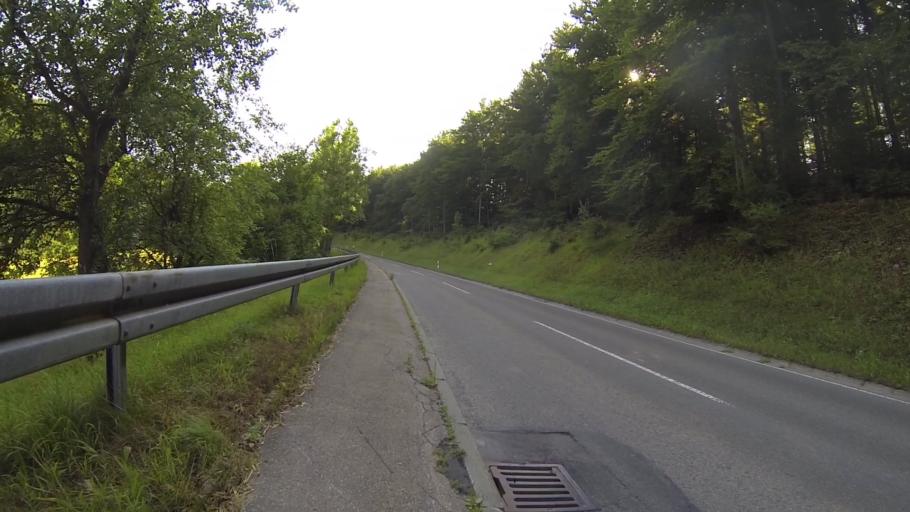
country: DE
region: Baden-Wuerttemberg
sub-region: Regierungsbezirk Stuttgart
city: Konigsbronn
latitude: 48.7377
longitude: 10.1410
